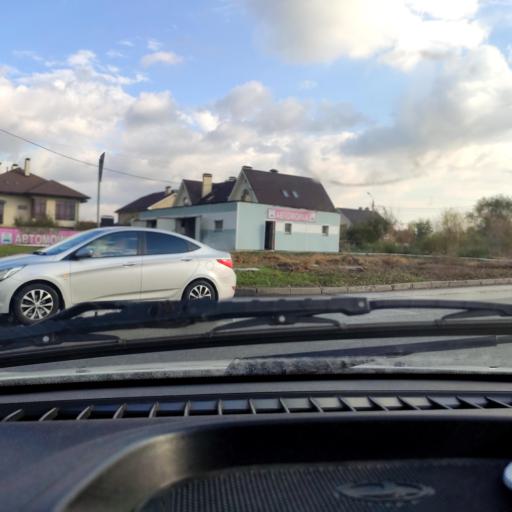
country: RU
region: Samara
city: Tol'yatti
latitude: 53.5407
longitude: 49.4155
